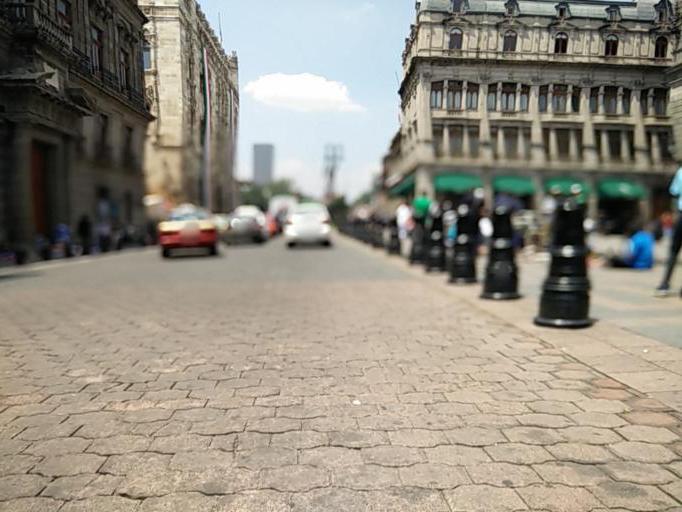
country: MX
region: Mexico City
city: Cuauhtemoc
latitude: 19.4359
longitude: -99.1395
